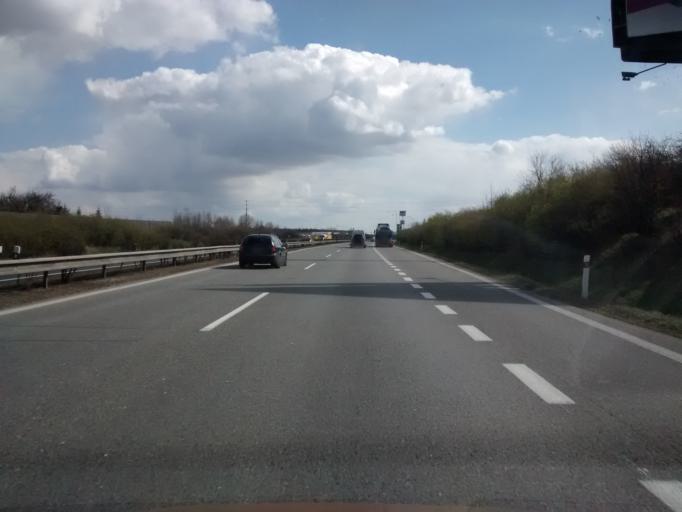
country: CZ
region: Central Bohemia
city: Odolena Voda
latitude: 50.2105
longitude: 14.4317
